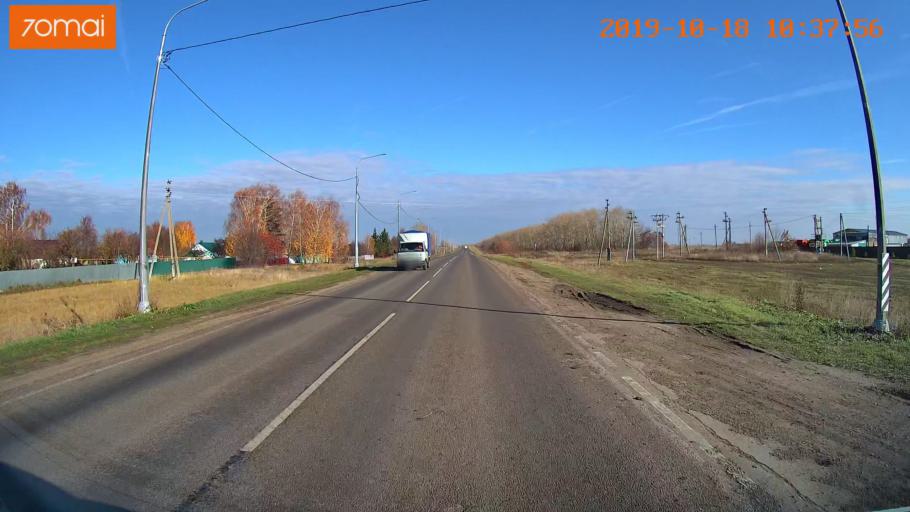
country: RU
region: Tula
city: Kurkino
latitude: 53.5667
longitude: 38.6362
